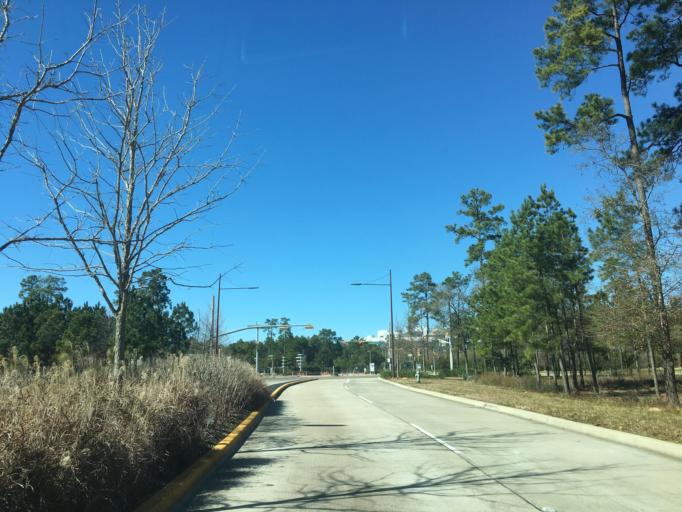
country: US
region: Texas
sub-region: Harris County
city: Spring
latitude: 30.0979
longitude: -95.4455
